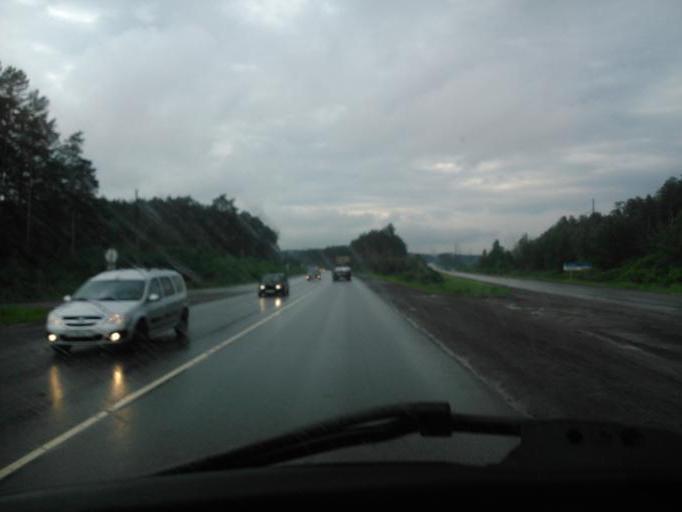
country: RU
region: Sverdlovsk
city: Beryozovsky
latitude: 56.9139
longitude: 60.7582
